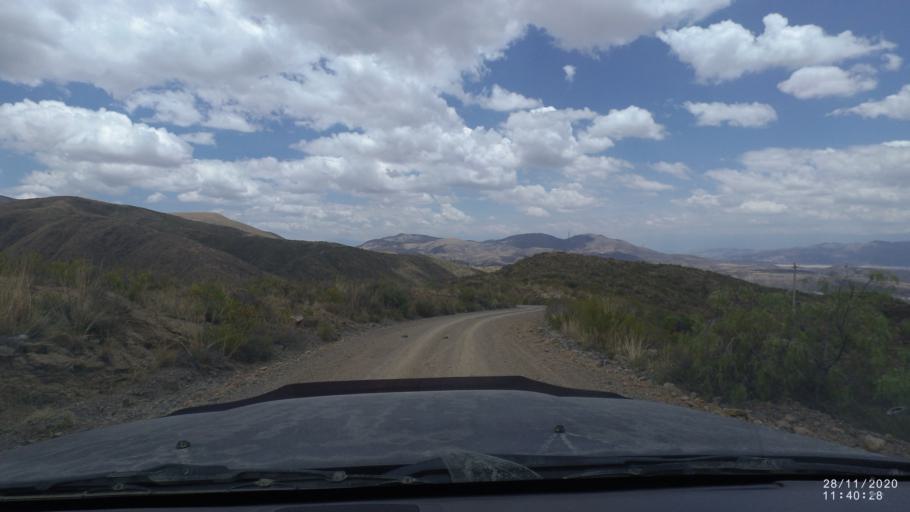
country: BO
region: Cochabamba
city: Tarata
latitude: -17.6740
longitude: -66.0468
